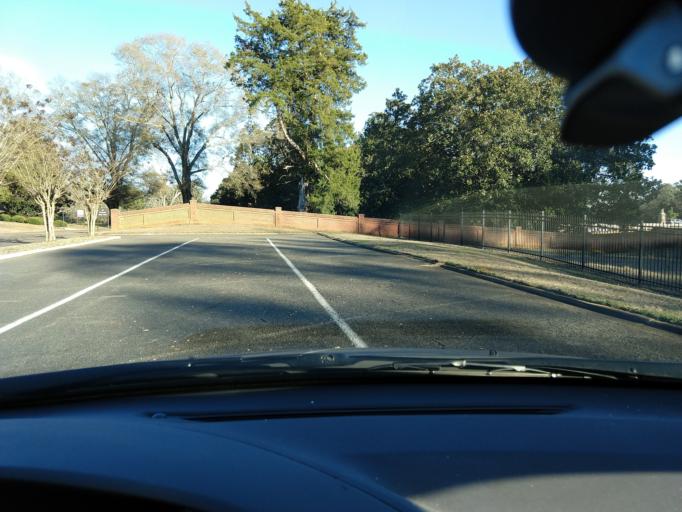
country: US
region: Georgia
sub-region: Macon County
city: Oglethorpe
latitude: 32.2033
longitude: -84.1332
